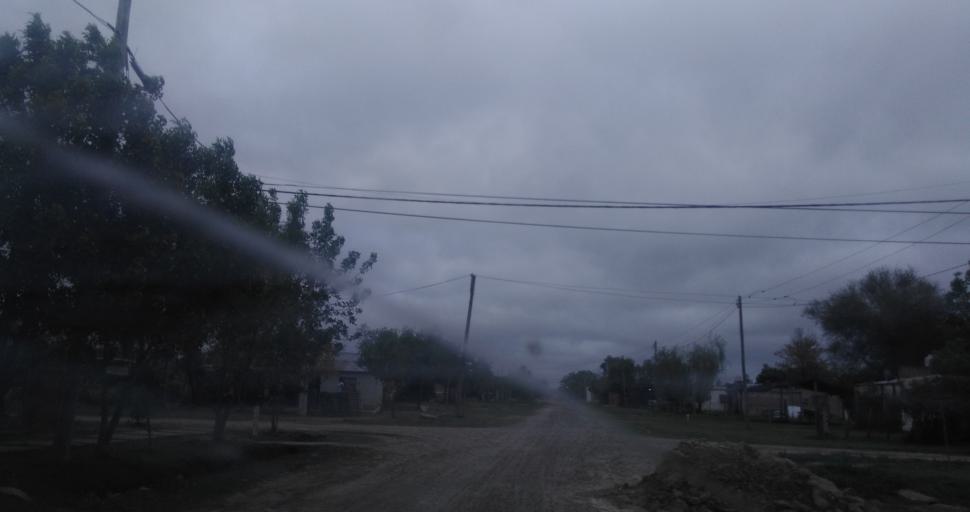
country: AR
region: Chaco
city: Resistencia
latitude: -27.4844
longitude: -58.9989
